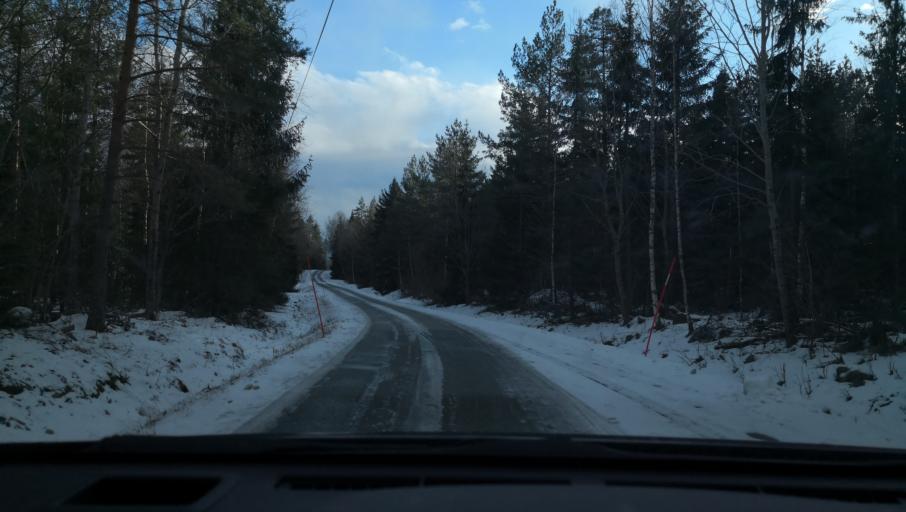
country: SE
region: Uppsala
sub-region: Enkopings Kommun
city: Irsta
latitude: 59.7020
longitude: 16.8689
